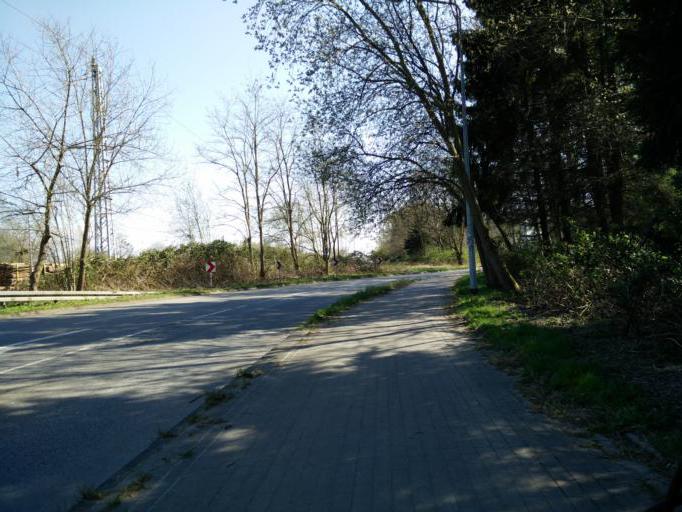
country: DE
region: Mecklenburg-Vorpommern
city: Rostock
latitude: 54.1060
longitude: 12.0856
